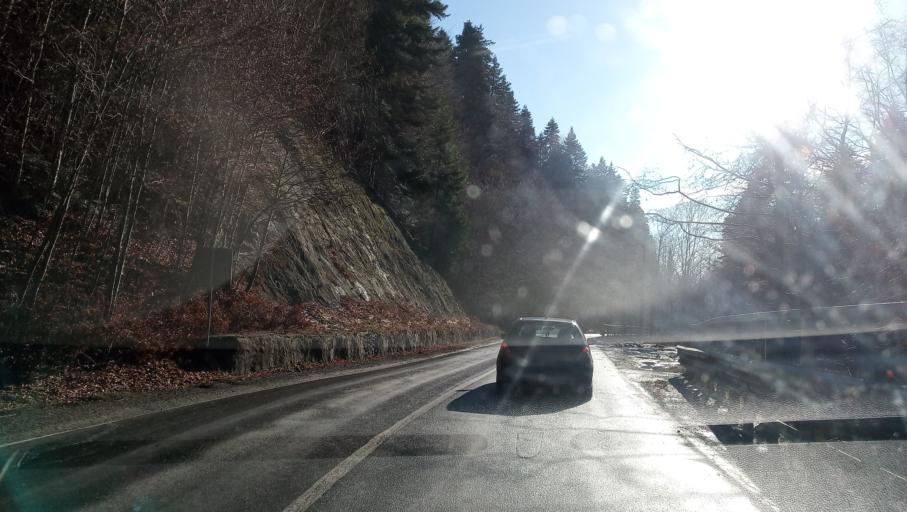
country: RO
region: Brasov
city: Crivina
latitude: 45.4718
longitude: 25.9290
